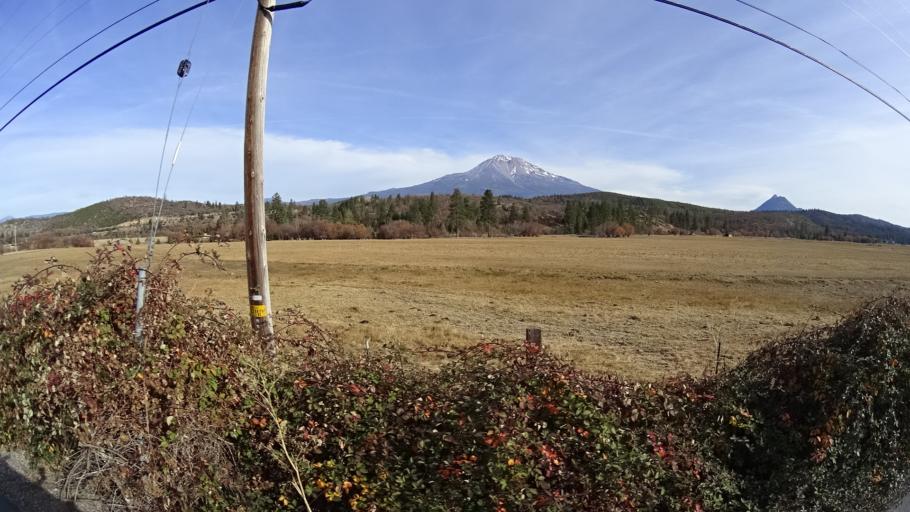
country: US
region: California
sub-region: Siskiyou County
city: Weed
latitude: 41.4292
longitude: -122.4372
